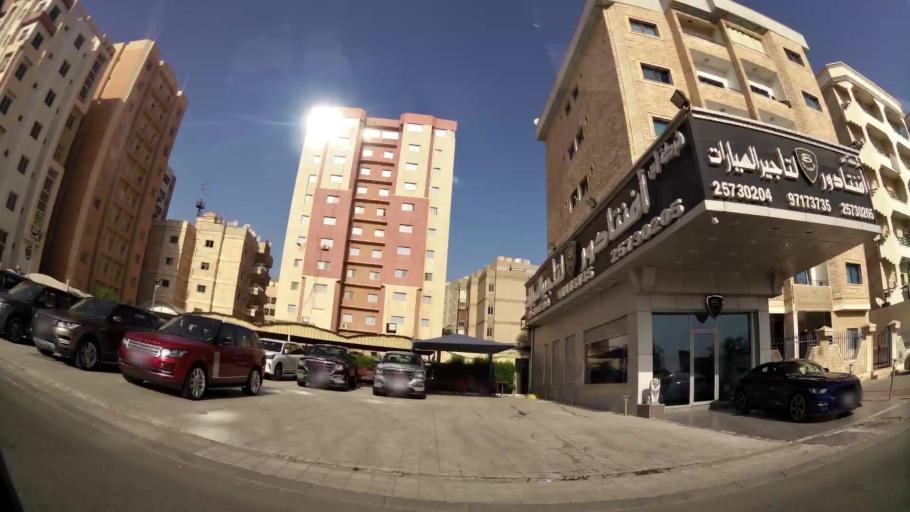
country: KW
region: Muhafazat Hawalli
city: As Salimiyah
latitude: 29.3273
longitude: 48.0845
